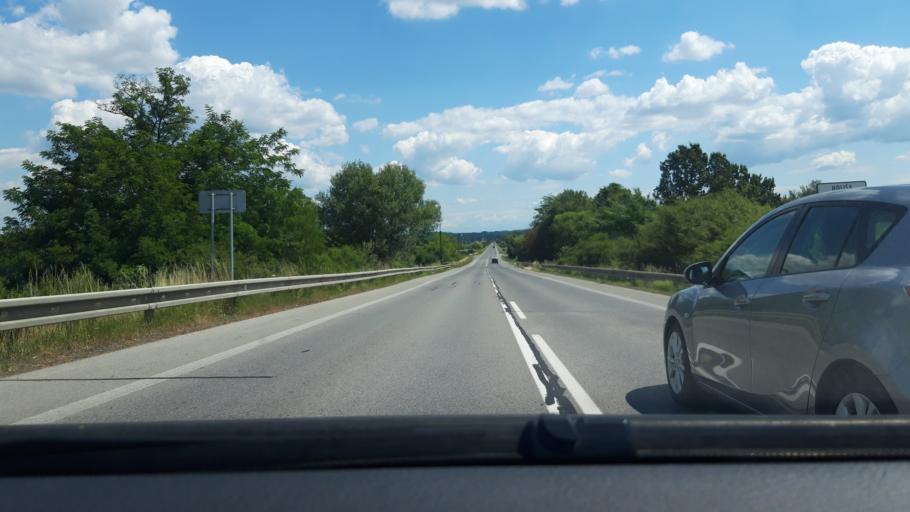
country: SK
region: Banskobystricky
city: Lucenec
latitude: 48.3068
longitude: 19.7191
